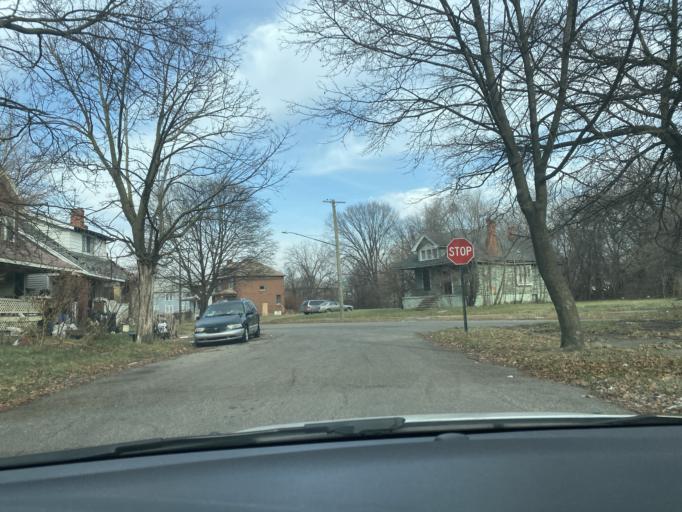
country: US
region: Michigan
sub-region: Wayne County
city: Highland Park
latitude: 42.3654
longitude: -83.1235
